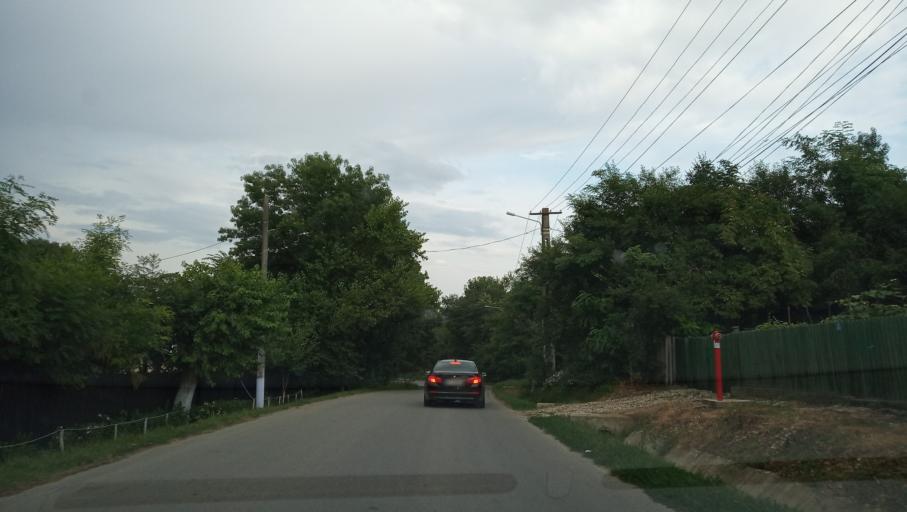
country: RO
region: Giurgiu
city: Iepuresti
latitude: 44.2566
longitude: 25.8899
